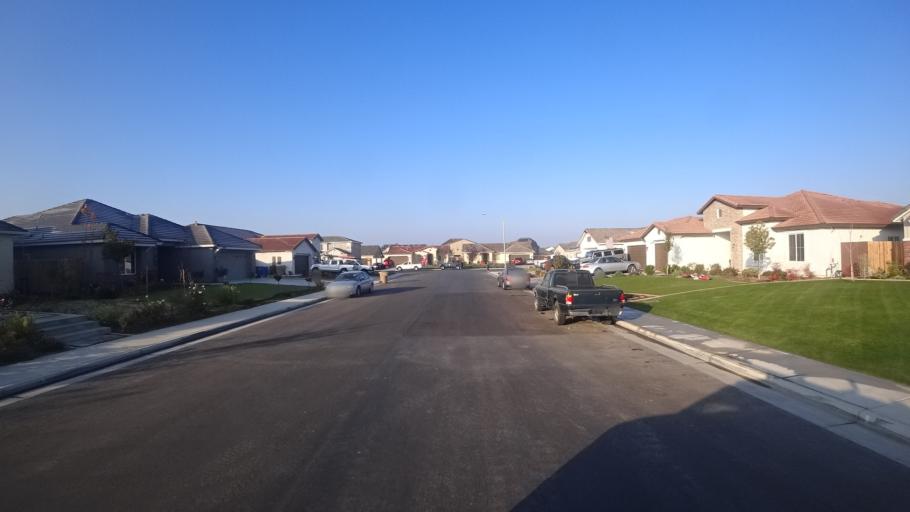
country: US
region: California
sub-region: Kern County
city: Greenacres
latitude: 35.2904
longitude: -119.1131
